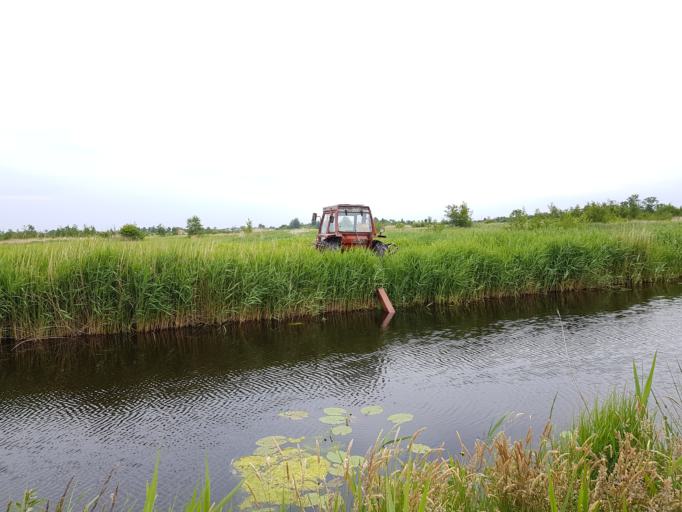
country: NL
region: Friesland
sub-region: Gemeente Boarnsterhim
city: Warten
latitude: 53.1375
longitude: 5.9223
